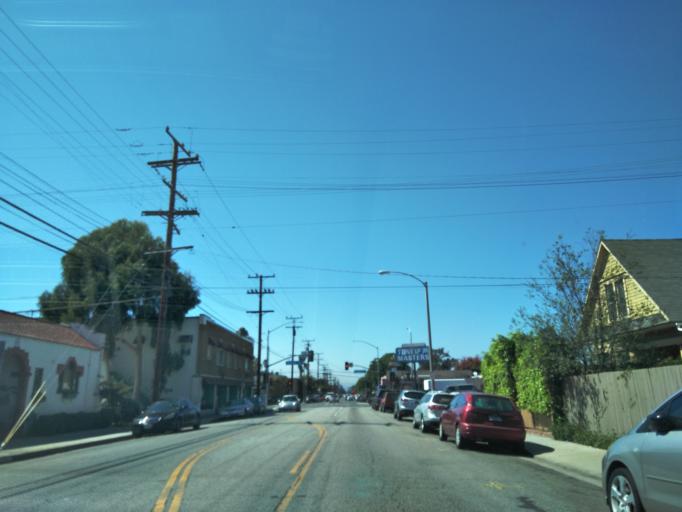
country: US
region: California
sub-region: Los Angeles County
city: Signal Hill
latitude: 33.7718
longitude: -118.1516
